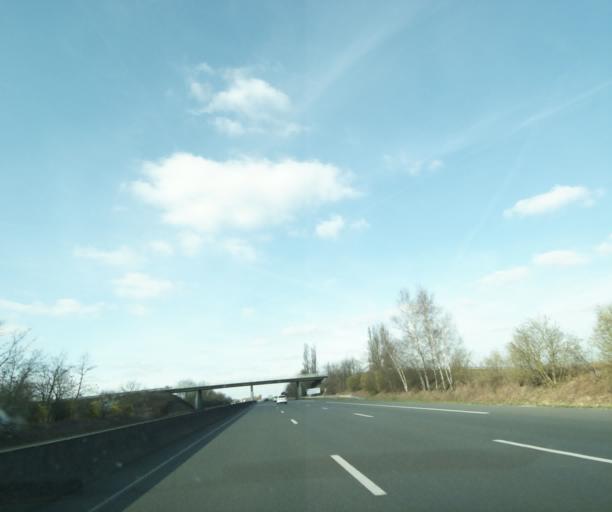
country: FR
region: Centre
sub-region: Departement d'Eure-et-Loir
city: Janville
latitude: 48.1770
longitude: 1.8542
